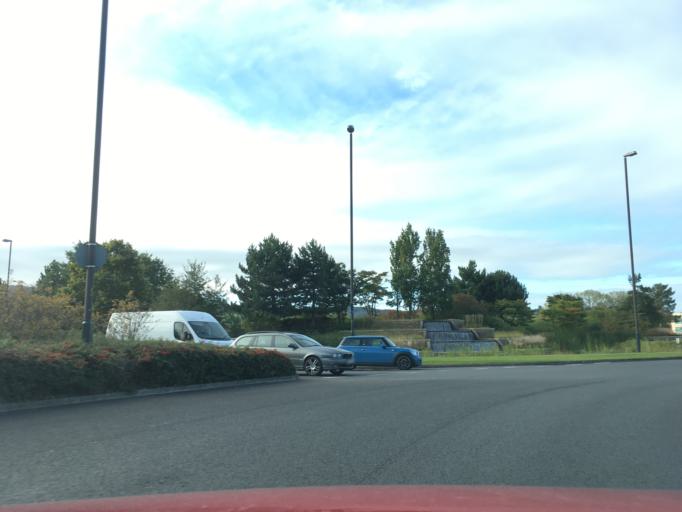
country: GB
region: England
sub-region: Gloucestershire
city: Churchdown
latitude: 51.8476
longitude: -2.1744
